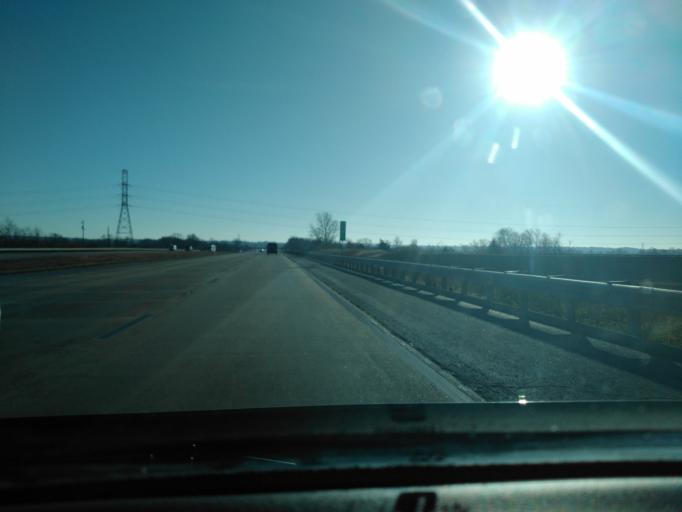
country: US
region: Missouri
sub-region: Saint Louis County
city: Oakville
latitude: 38.4819
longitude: -90.2600
